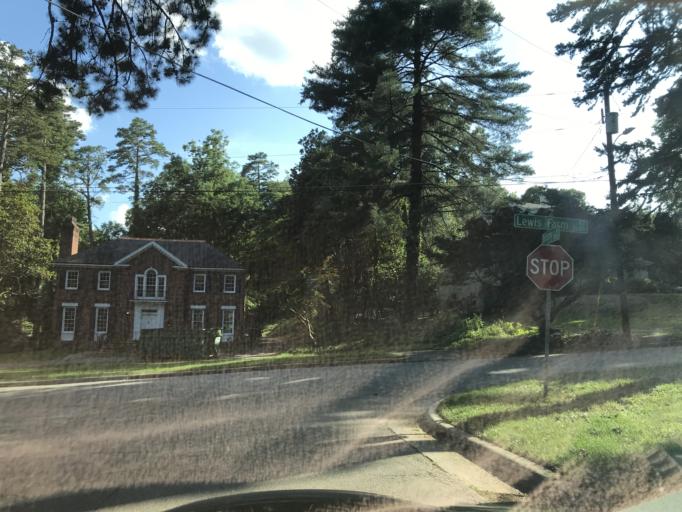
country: US
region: North Carolina
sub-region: Wake County
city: West Raleigh
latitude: 35.8079
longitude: -78.6667
